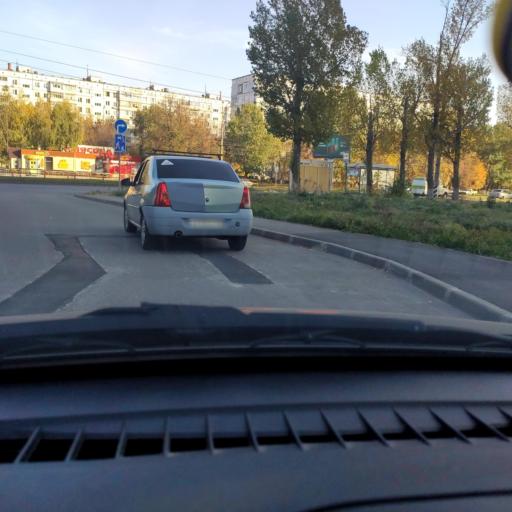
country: RU
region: Samara
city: Tol'yatti
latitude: 53.5188
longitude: 49.2578
